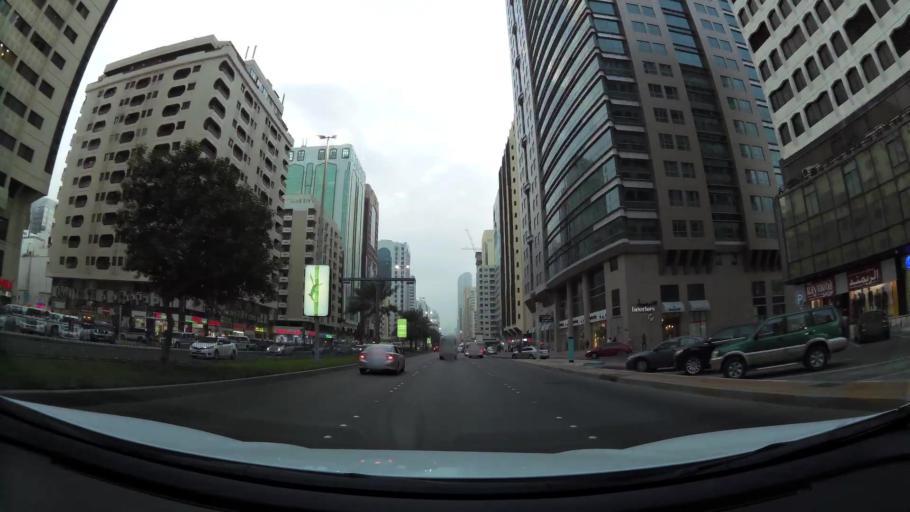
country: AE
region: Abu Dhabi
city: Abu Dhabi
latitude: 24.4954
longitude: 54.3710
